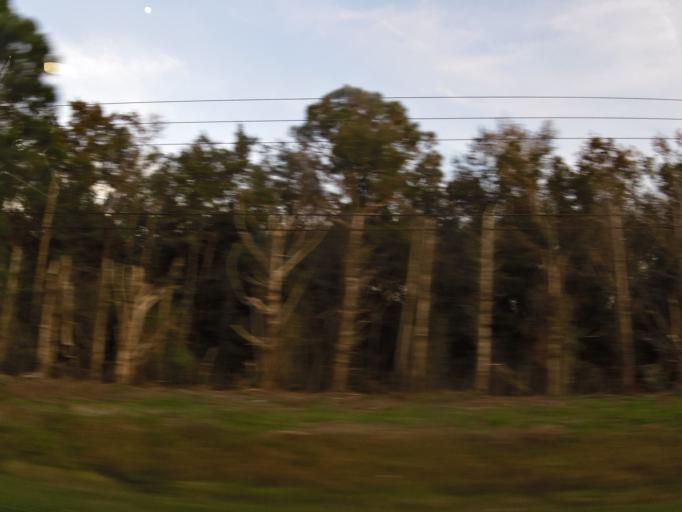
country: US
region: Florida
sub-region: Volusia County
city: North DeLand
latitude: 29.0852
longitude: -81.3043
